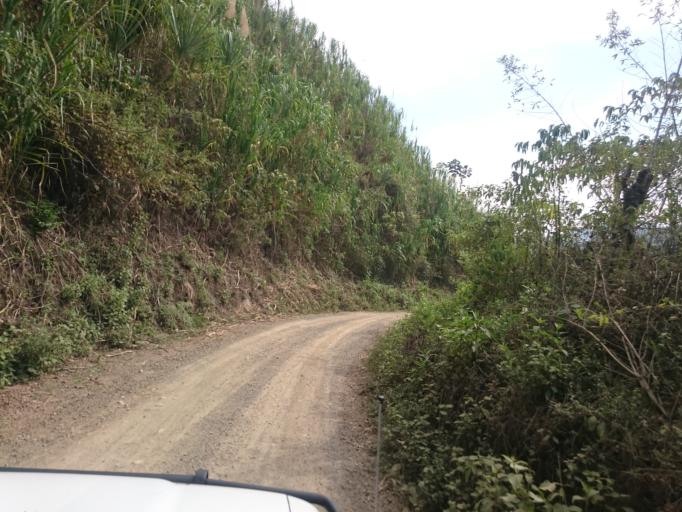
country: CO
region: Cauca
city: Suarez
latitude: 2.9367
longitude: -76.7170
